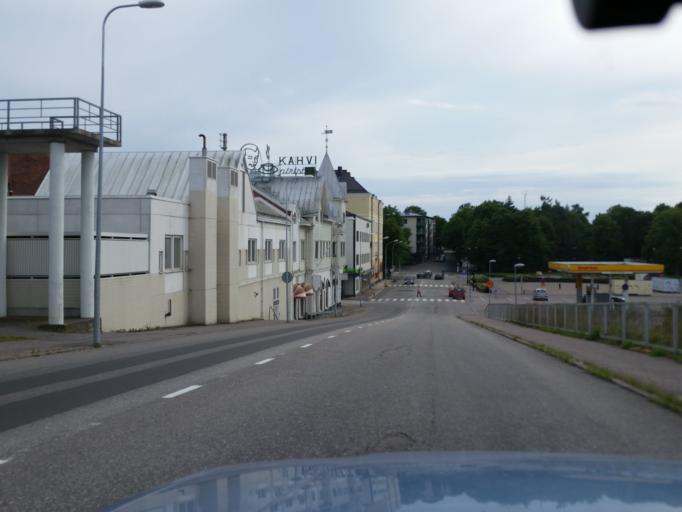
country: FI
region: Uusimaa
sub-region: Raaseporin
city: Hanko
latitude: 59.8257
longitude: 22.9652
